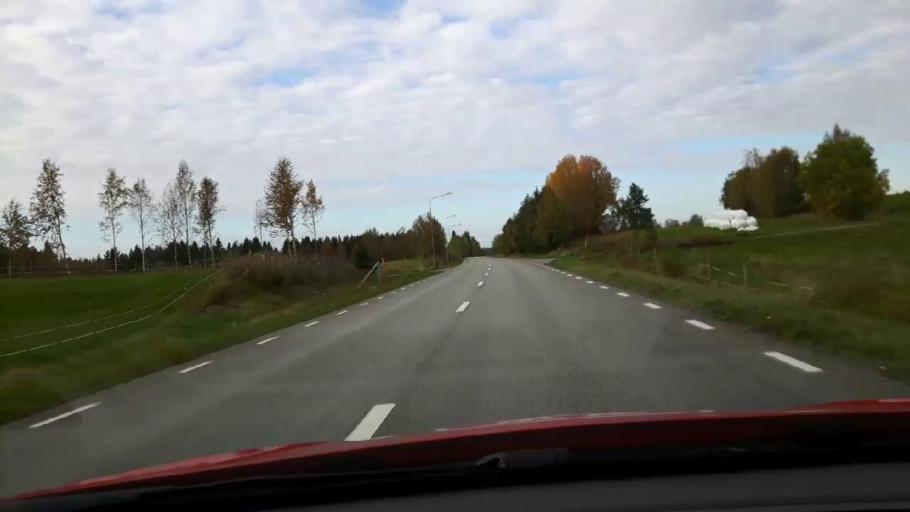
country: SE
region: Jaemtland
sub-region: Krokoms Kommun
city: Valla
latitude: 63.2368
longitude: 14.0069
